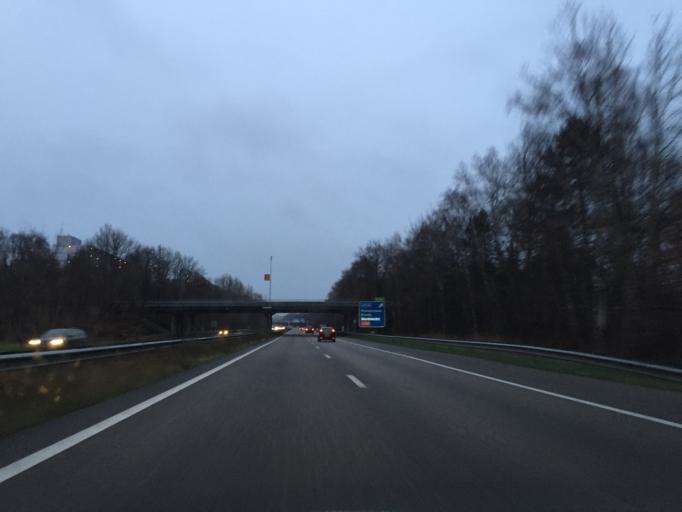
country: NL
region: North Brabant
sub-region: Gemeente Bergen op Zoom
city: Bergen op Zoom
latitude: 51.4879
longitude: 4.3167
